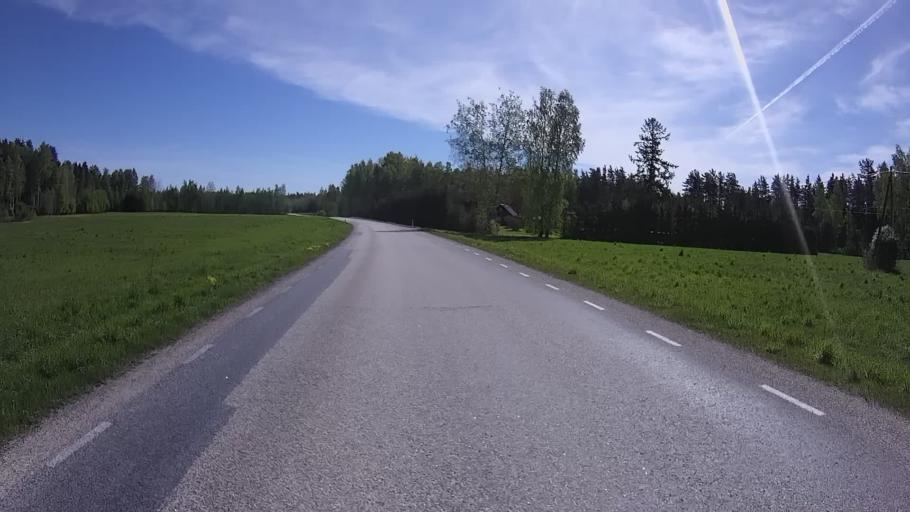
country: EE
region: Polvamaa
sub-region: Raepina vald
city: Rapina
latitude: 57.9666
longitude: 27.5351
